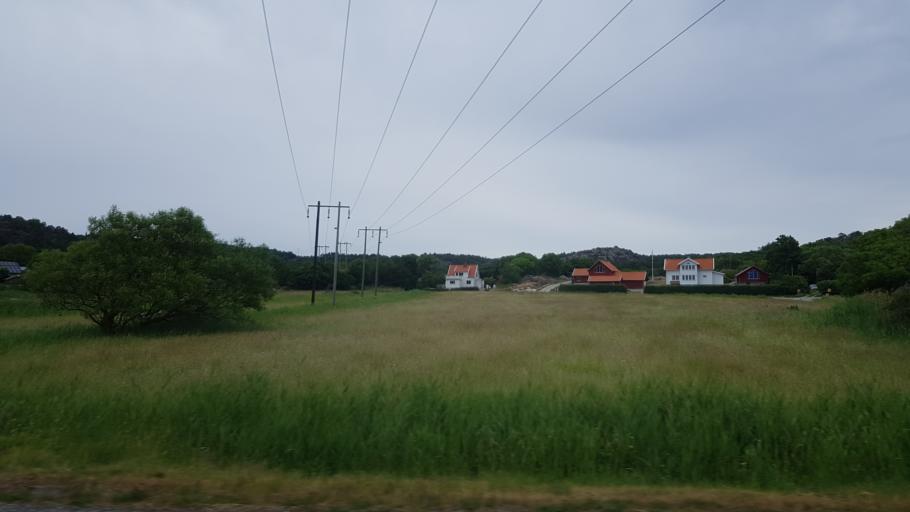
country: SE
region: Vaestra Goetaland
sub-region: Tjorns Kommun
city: Skaerhamn
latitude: 57.9631
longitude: 11.5756
